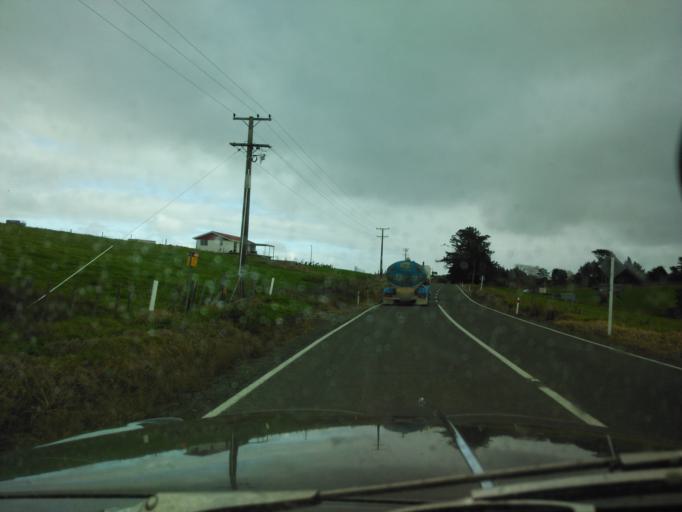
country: NZ
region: Auckland
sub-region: Auckland
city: Wellsford
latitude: -36.1440
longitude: 174.4946
